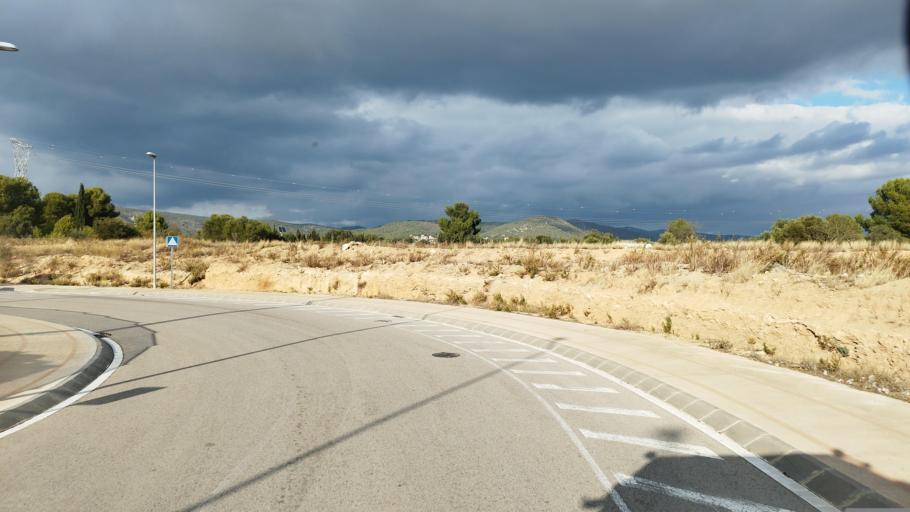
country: ES
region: Catalonia
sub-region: Provincia de Tarragona
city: la Bisbal del Penedes
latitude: 41.2745
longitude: 1.5170
